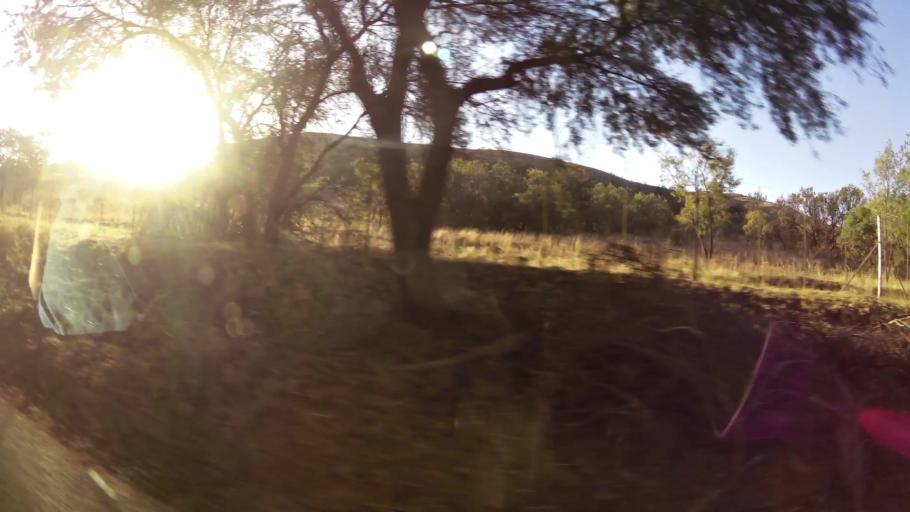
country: ZA
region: Gauteng
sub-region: City of Tshwane Metropolitan Municipality
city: Pretoria
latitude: -25.6959
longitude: 28.2325
